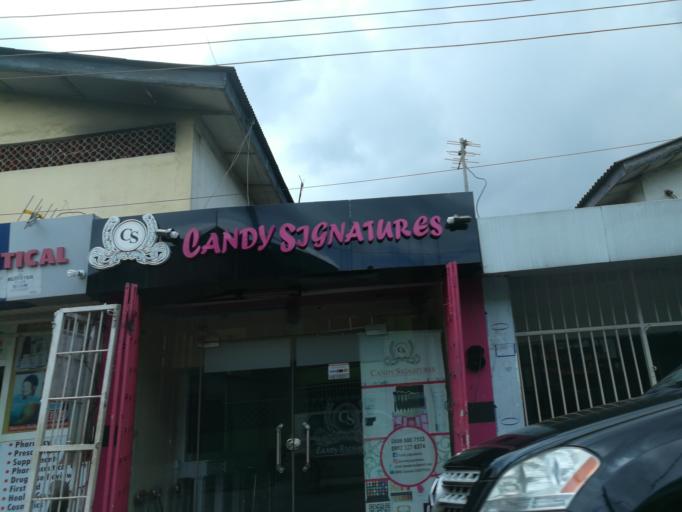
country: NG
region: Lagos
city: Ikeja
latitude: 6.5983
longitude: 3.3499
